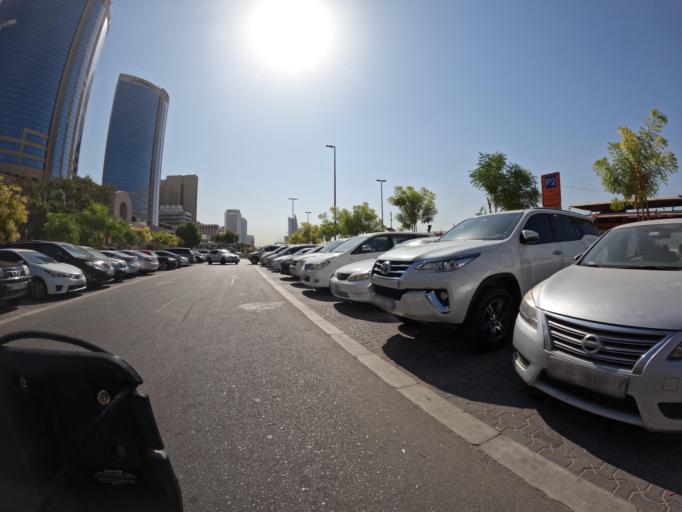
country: AE
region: Ash Shariqah
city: Sharjah
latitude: 25.2664
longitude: 55.3071
